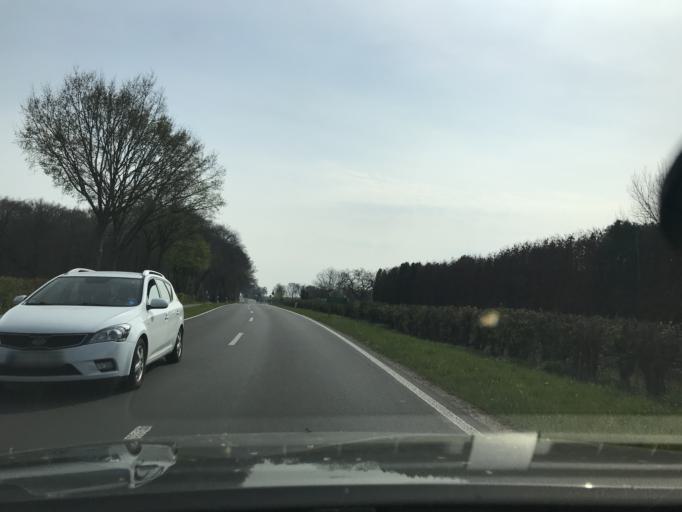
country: DE
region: North Rhine-Westphalia
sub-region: Regierungsbezirk Dusseldorf
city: Kleve
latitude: 51.7438
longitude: 6.1681
